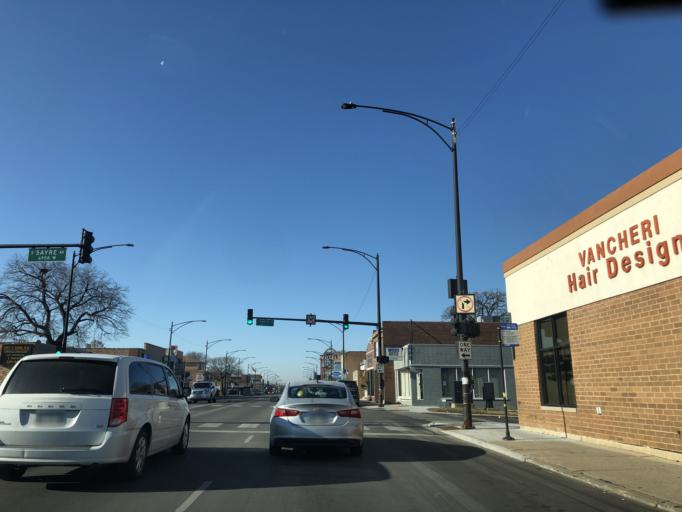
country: US
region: Illinois
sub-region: Cook County
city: Summit
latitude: 41.7921
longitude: -87.7960
